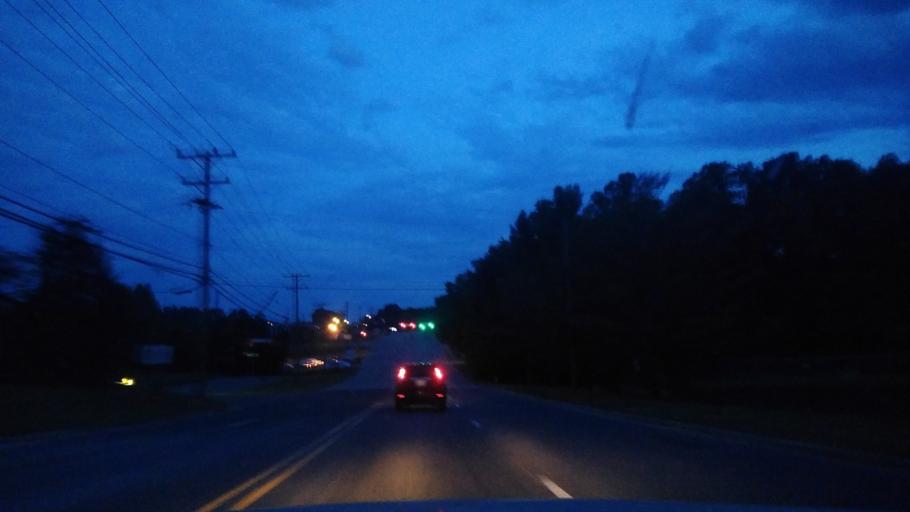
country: US
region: North Carolina
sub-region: Guilford County
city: Jamestown
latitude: 36.0724
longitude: -79.9101
